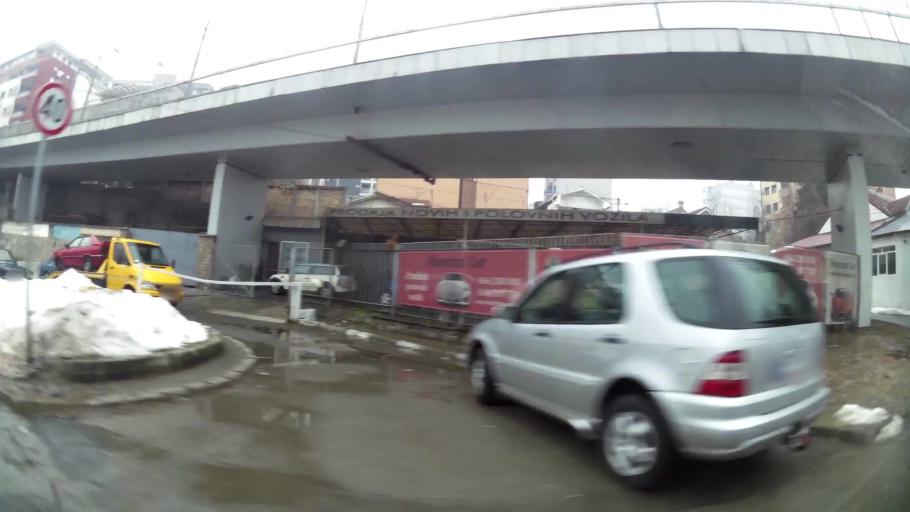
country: RS
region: Central Serbia
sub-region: Belgrade
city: Cukarica
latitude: 44.7852
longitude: 20.4220
